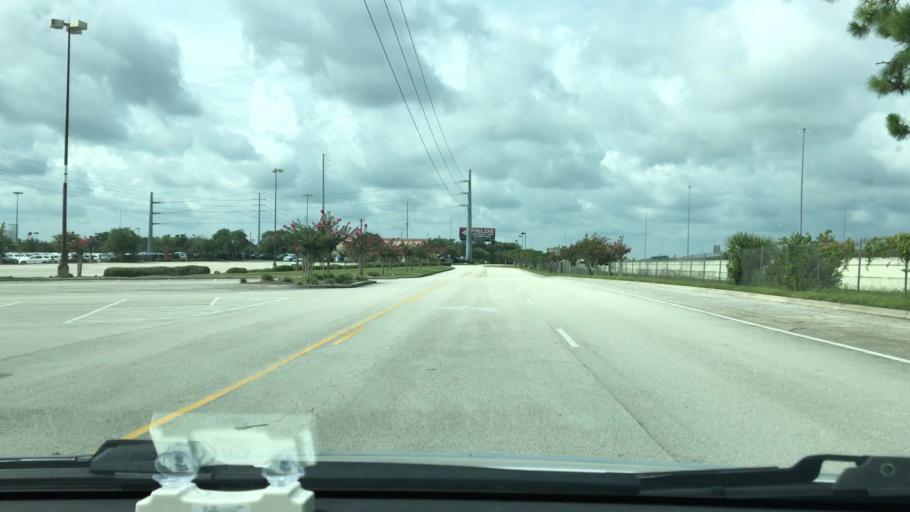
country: US
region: Florida
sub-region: Seminole County
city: Lake Mary
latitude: 28.8025
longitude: -81.3413
